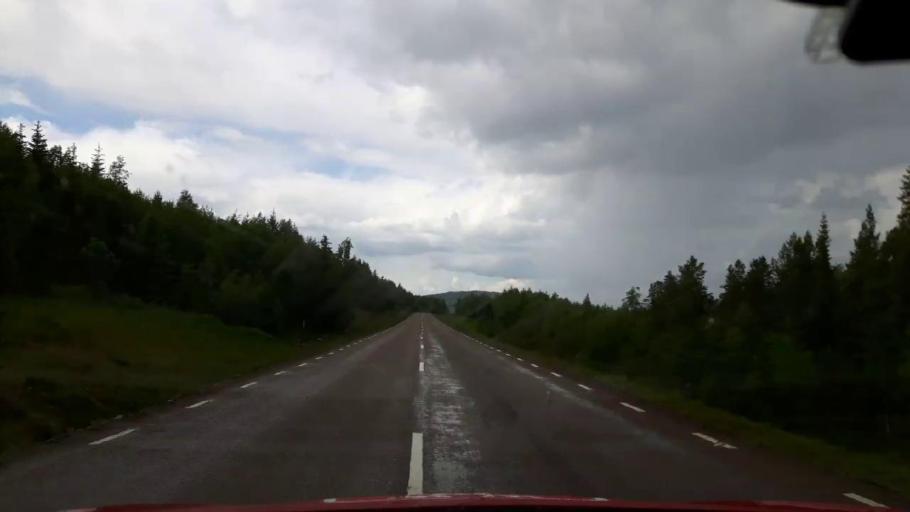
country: SE
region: Jaemtland
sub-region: Krokoms Kommun
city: Valla
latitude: 63.8902
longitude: 14.2713
